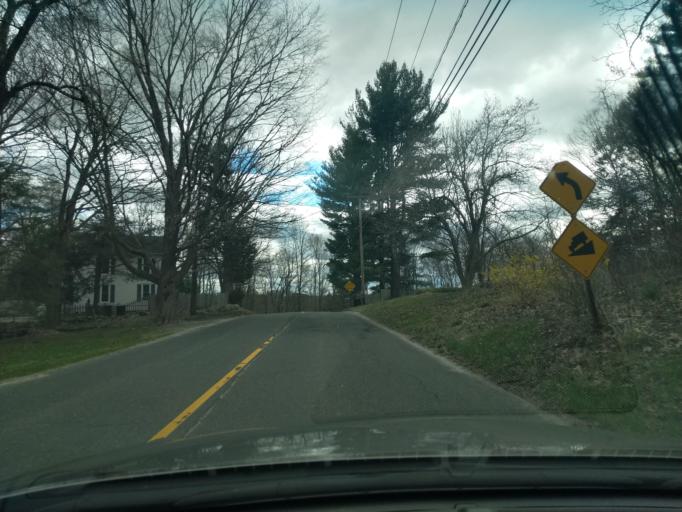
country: US
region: Connecticut
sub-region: Fairfield County
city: Bethel
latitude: 41.3856
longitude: -73.3734
